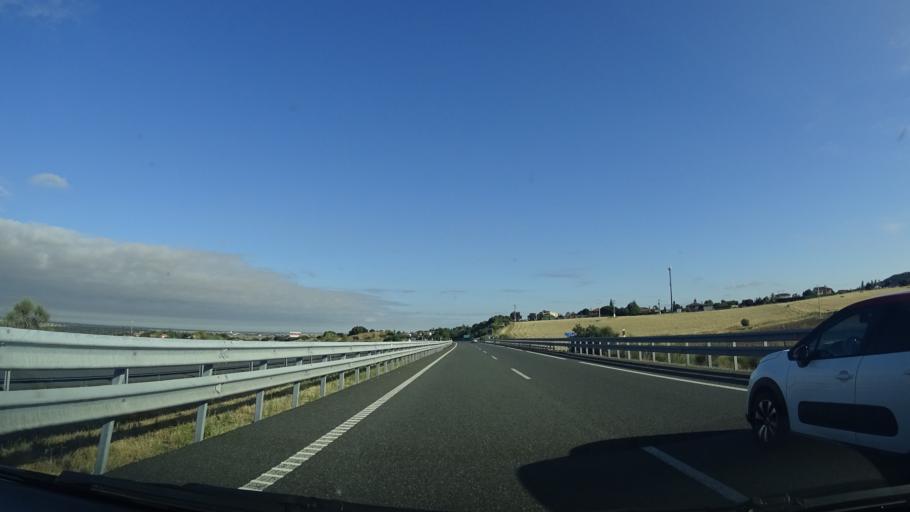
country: ES
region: Castille and Leon
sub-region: Provincia de Segovia
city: Labajos
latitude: 40.8508
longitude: -4.5442
